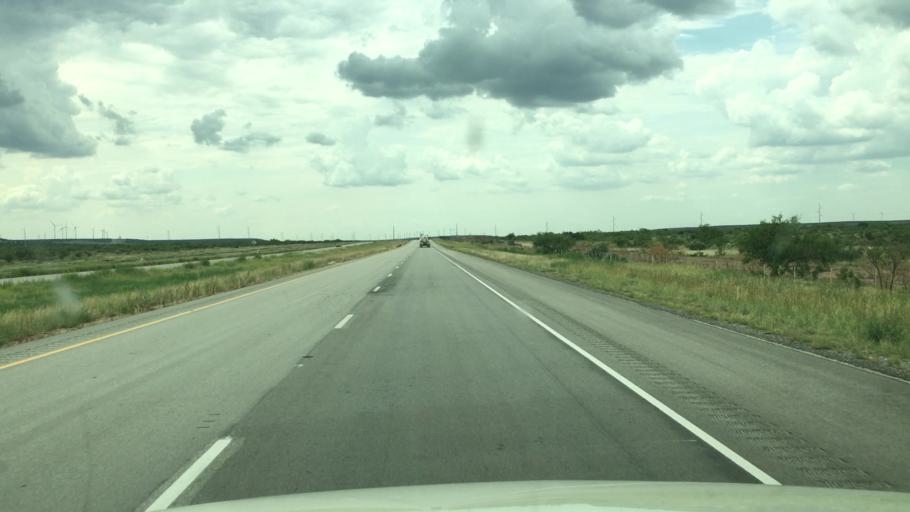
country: US
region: Texas
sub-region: Sterling County
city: Sterling City
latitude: 31.9548
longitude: -101.1935
